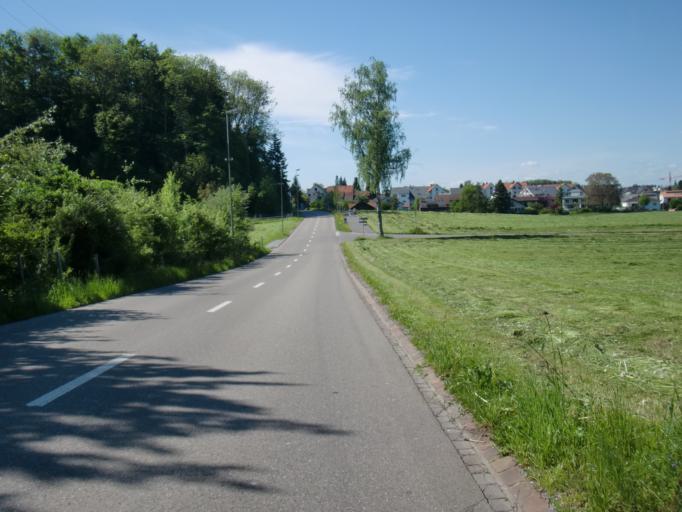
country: CH
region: Zurich
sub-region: Bezirk Hinwil
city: Bubikon
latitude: 47.2648
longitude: 8.8240
